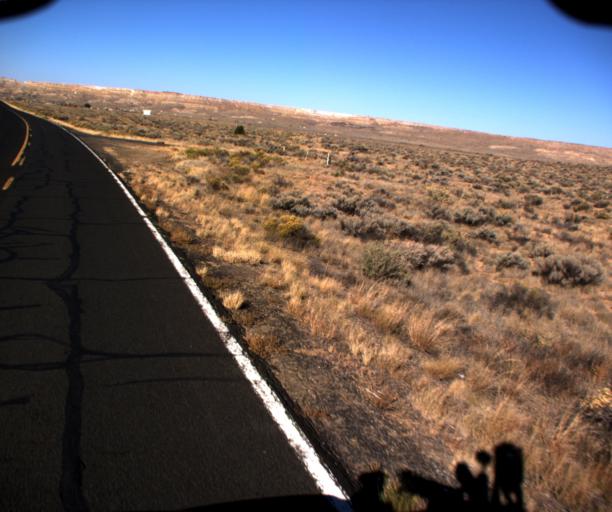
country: US
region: Arizona
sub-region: Navajo County
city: First Mesa
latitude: 35.8420
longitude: -110.3260
